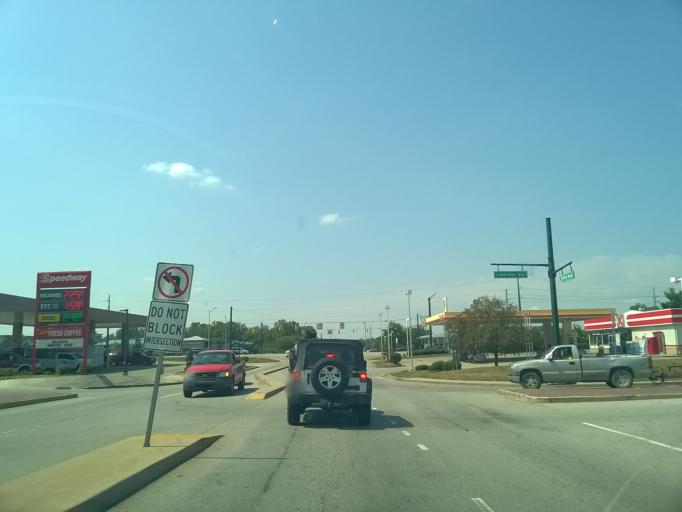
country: US
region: Indiana
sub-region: Hendricks County
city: Plainfield
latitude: 39.6751
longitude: -86.3698
